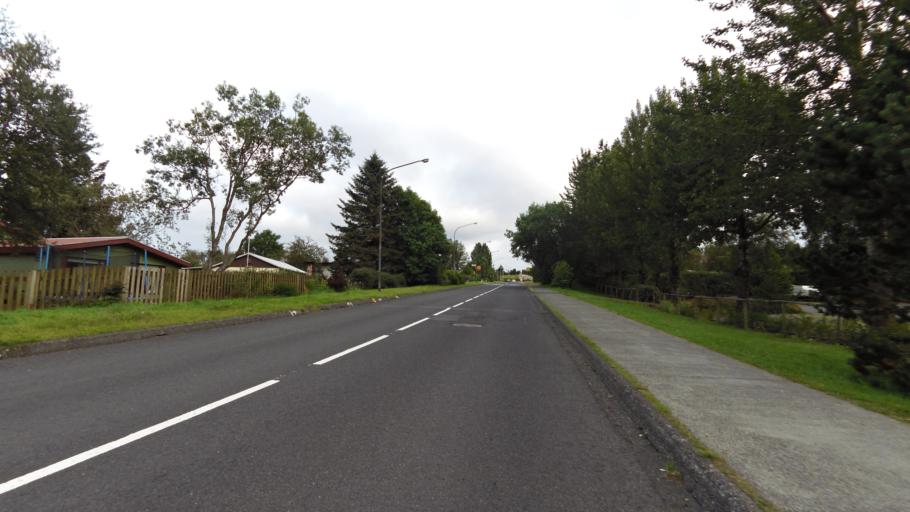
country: IS
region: Capital Region
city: Reykjavik
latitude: 64.1167
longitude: -21.8487
